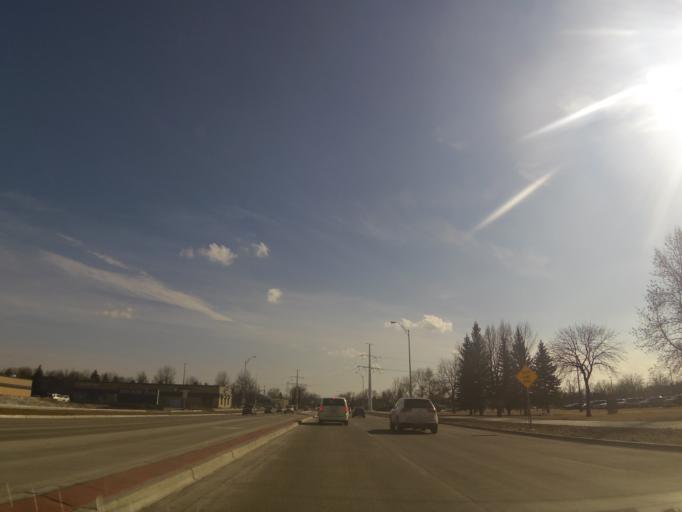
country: US
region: North Dakota
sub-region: Grand Forks County
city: Grand Forks
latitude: 47.9088
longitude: -97.0665
